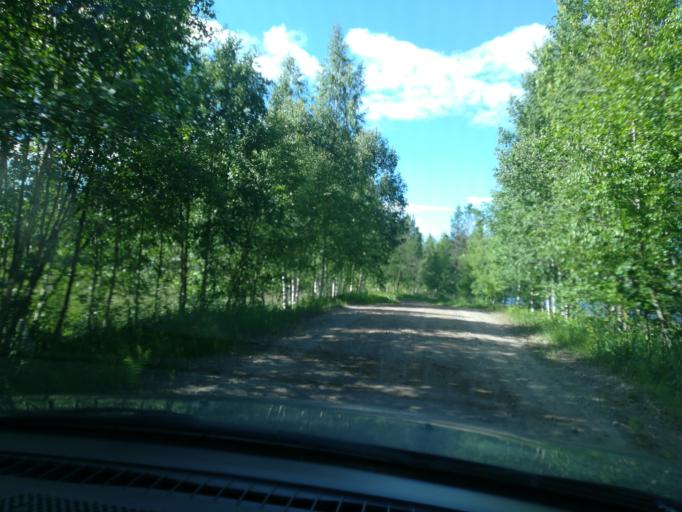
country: FI
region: Southern Savonia
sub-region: Mikkeli
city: Puumala
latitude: 61.6630
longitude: 28.1495
